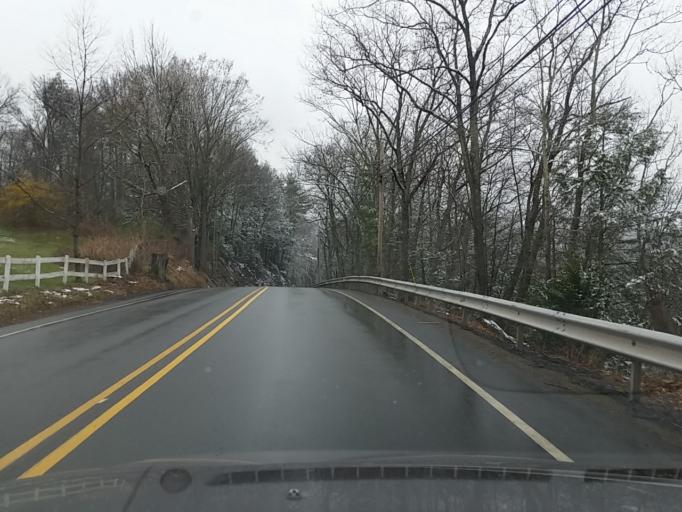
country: US
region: Pennsylvania
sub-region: Columbia County
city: Light Street
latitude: 41.1981
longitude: -76.3765
